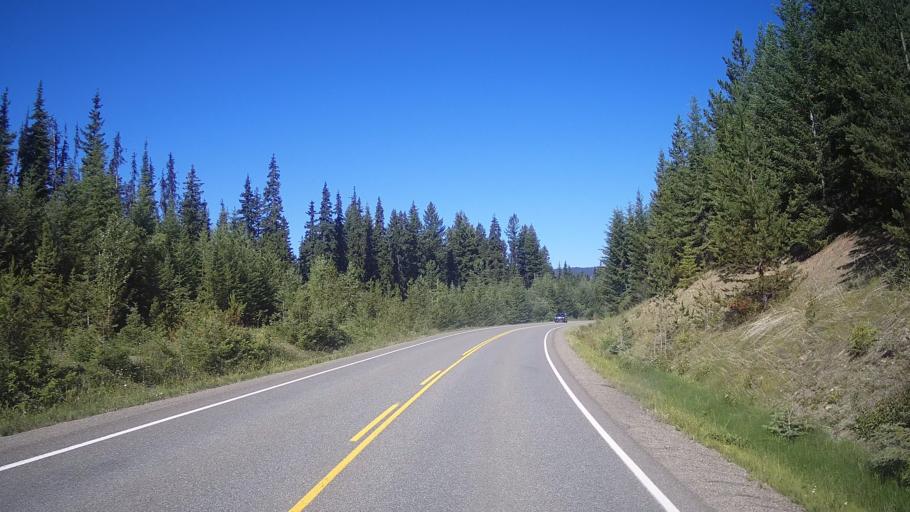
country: CA
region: British Columbia
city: Kamloops
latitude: 51.4969
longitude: -120.4298
